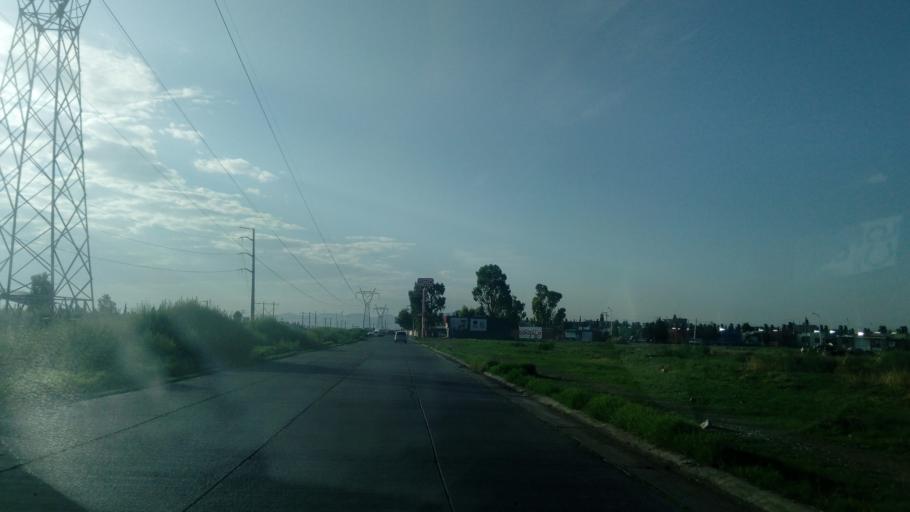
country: MX
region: Durango
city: Victoria de Durango
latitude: 24.0754
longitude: -104.5891
